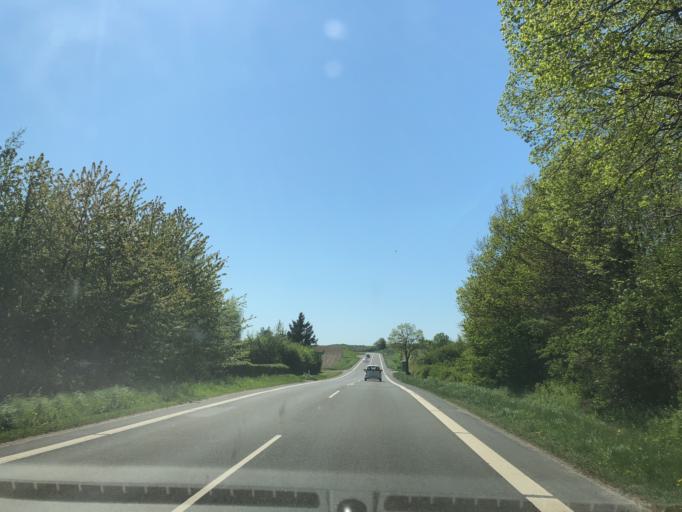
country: DK
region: Zealand
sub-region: Slagelse Kommune
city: Korsor
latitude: 55.3262
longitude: 11.1981
